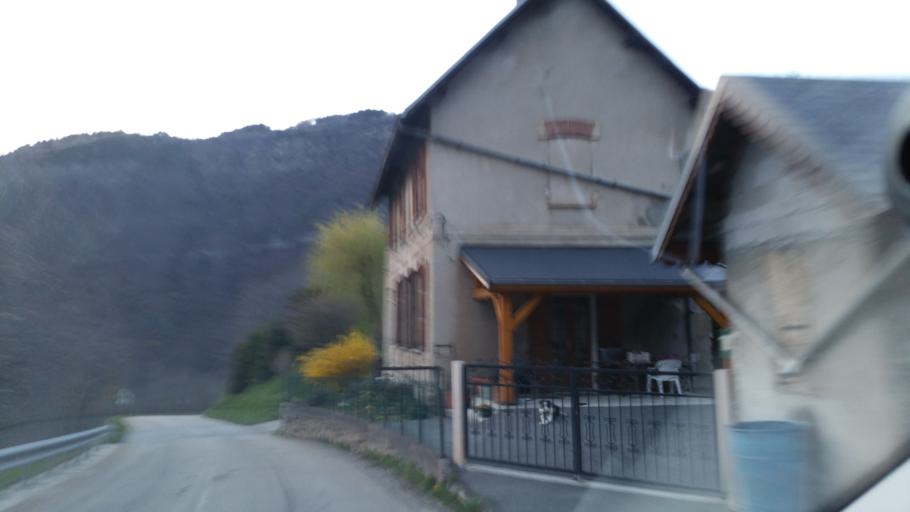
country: FR
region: Rhone-Alpes
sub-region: Departement de la Savoie
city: La Chambre
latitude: 45.3734
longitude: 6.3227
